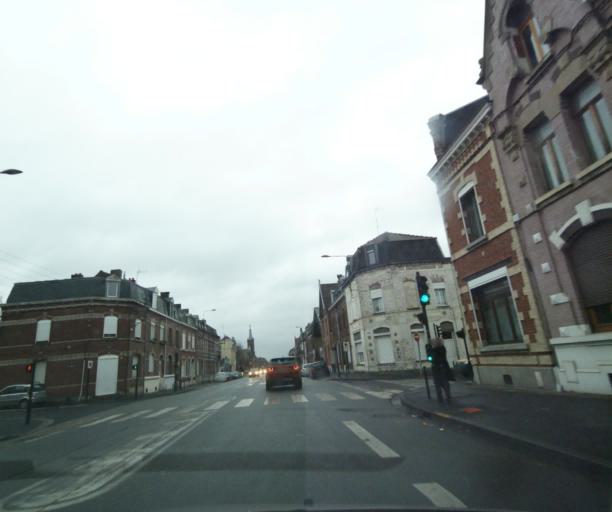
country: FR
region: Nord-Pas-de-Calais
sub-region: Departement du Nord
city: Anzin
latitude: 50.3604
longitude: 3.5067
